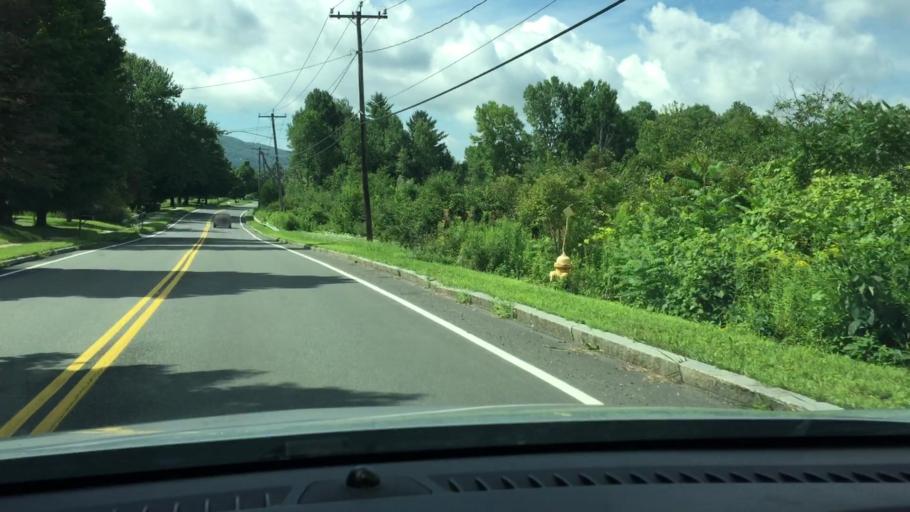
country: US
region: Massachusetts
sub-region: Berkshire County
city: Pittsfield
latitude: 42.4481
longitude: -73.2999
